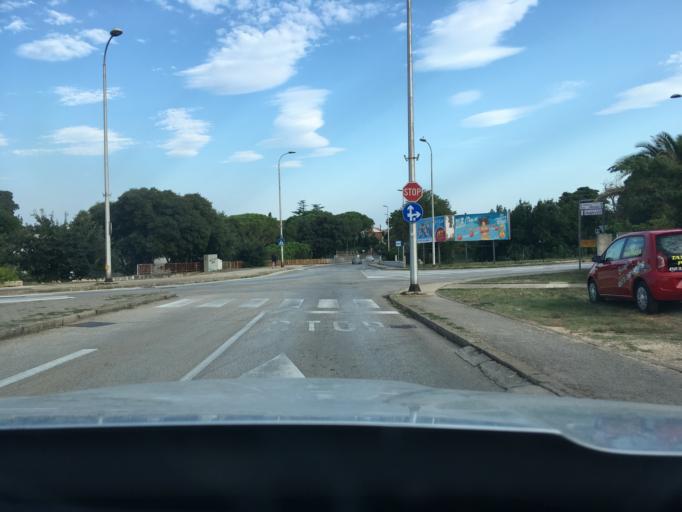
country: HR
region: Zadarska
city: Zadar
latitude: 44.1253
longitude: 15.2281
